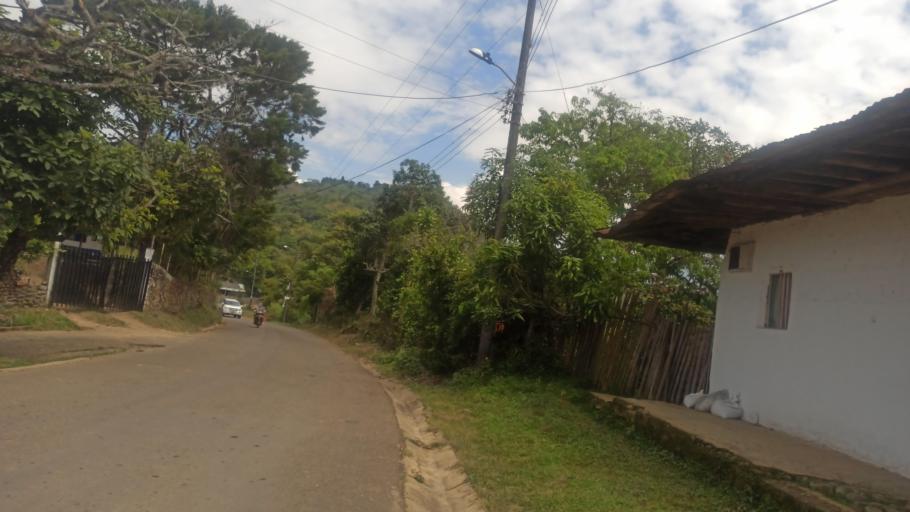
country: CO
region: Valle del Cauca
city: Jamundi
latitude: 3.1874
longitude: -76.6328
